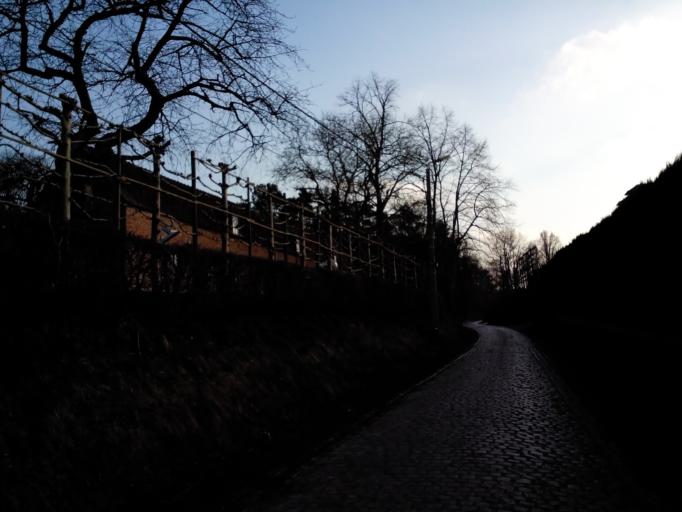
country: BE
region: Flanders
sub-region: Provincie Vlaams-Brabant
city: Oud-Heverlee
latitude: 50.8250
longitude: 4.6888
